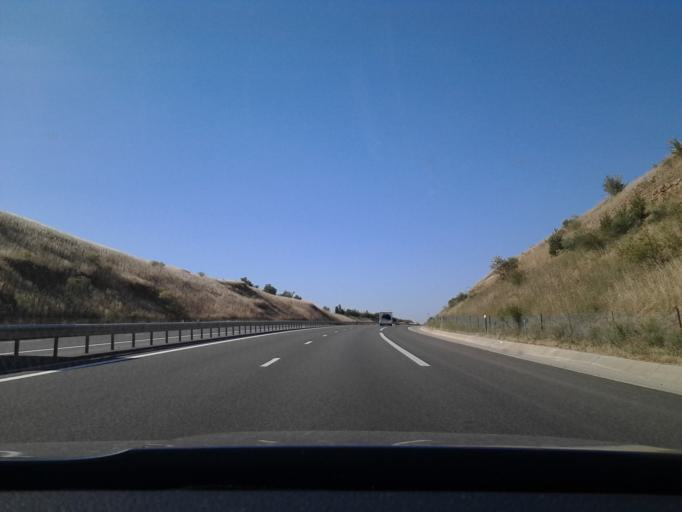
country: FR
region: Midi-Pyrenees
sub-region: Departement de l'Aveyron
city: Creissels
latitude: 44.1267
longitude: 3.0310
